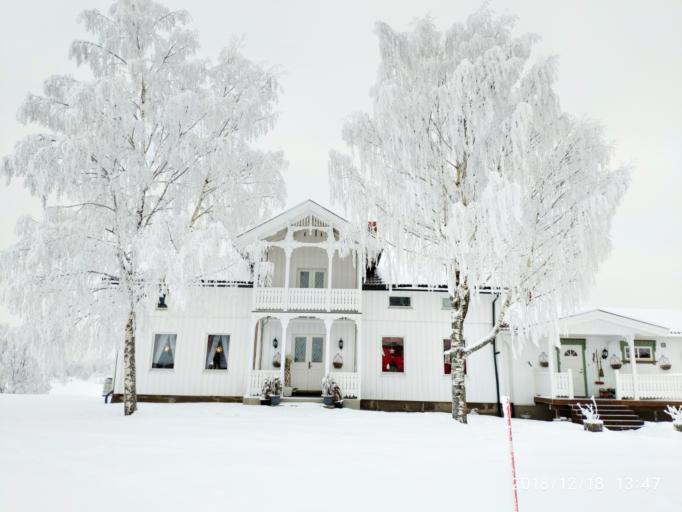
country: NO
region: Akershus
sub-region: Nannestad
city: Teigebyen
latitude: 60.1698
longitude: 11.0209
